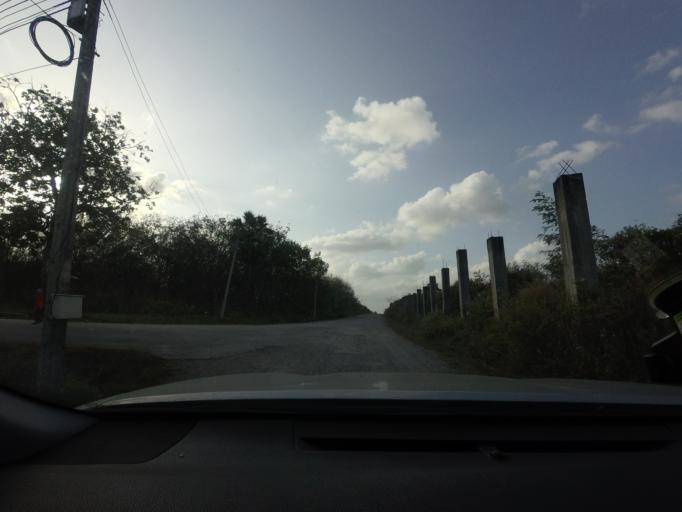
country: TH
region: Pattani
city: Mae Lan
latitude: 6.6159
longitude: 101.2560
